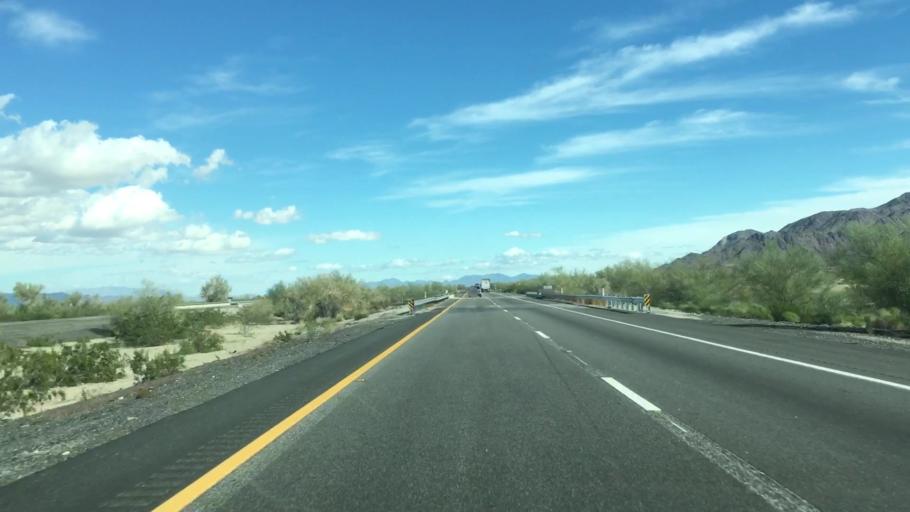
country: US
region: California
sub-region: Imperial County
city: Niland
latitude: 33.6826
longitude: -115.5405
